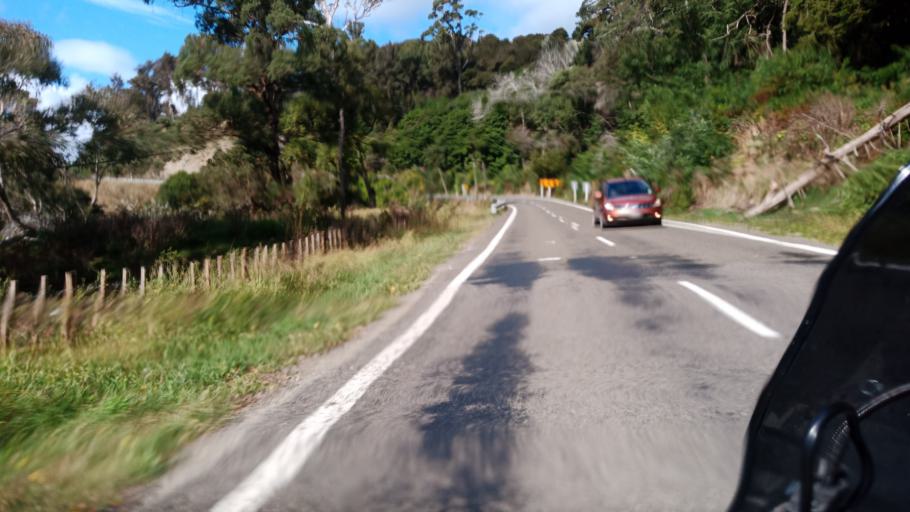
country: NZ
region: Gisborne
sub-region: Gisborne District
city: Gisborne
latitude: -38.4715
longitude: 177.6670
